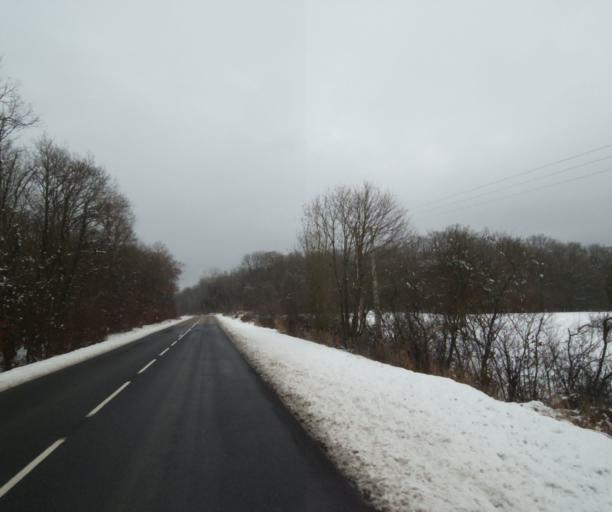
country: FR
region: Champagne-Ardenne
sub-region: Departement de la Haute-Marne
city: Laneuville-a-Remy
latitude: 48.4925
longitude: 4.8811
